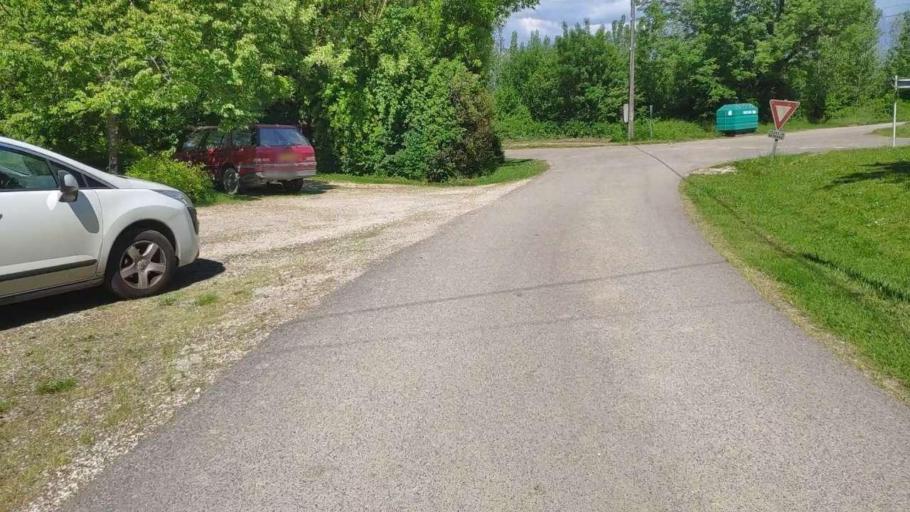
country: FR
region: Franche-Comte
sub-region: Departement du Jura
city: Bletterans
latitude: 46.7953
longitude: 5.4161
